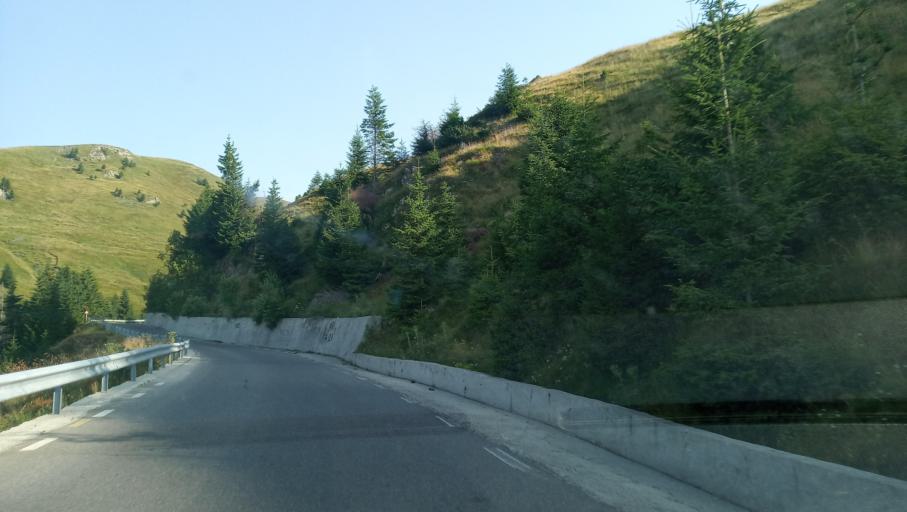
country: RO
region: Prahova
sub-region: Oras Sinaia
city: Sinaia
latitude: 45.3214
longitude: 25.4769
